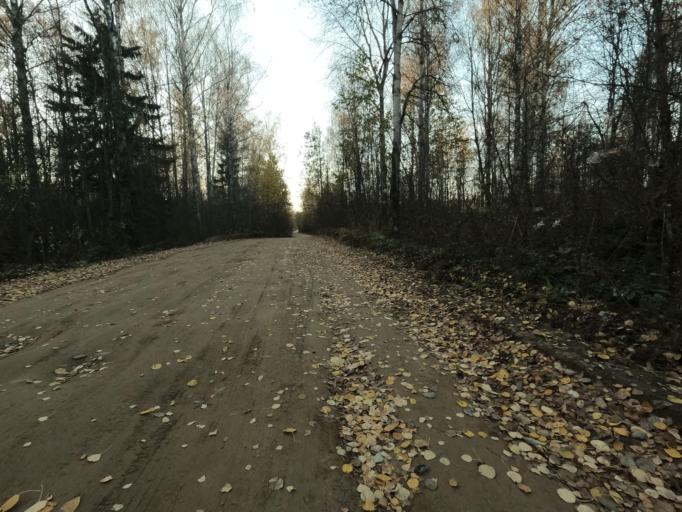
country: RU
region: Leningrad
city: Mga
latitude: 59.7548
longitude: 31.2811
